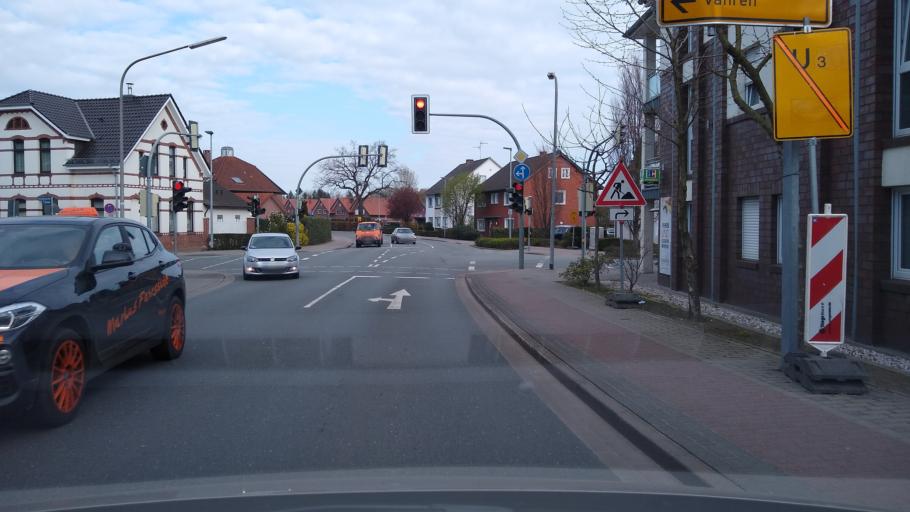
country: DE
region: Lower Saxony
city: Cloppenburg
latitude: 52.8416
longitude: 8.0340
